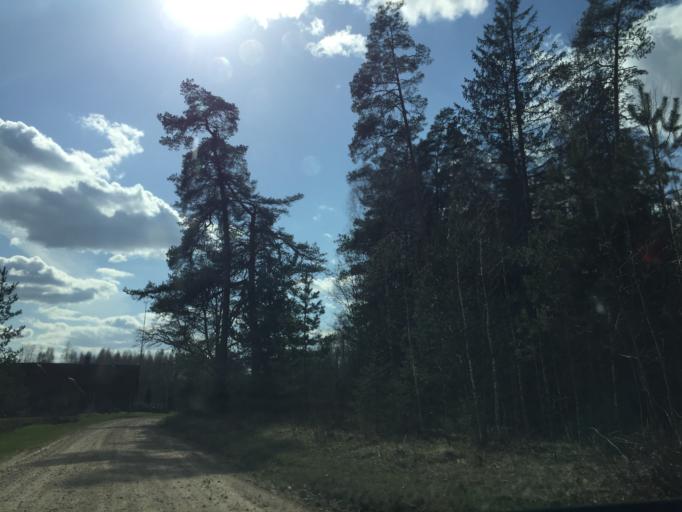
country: LV
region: Skriveri
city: Skriveri
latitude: 56.7846
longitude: 25.2354
